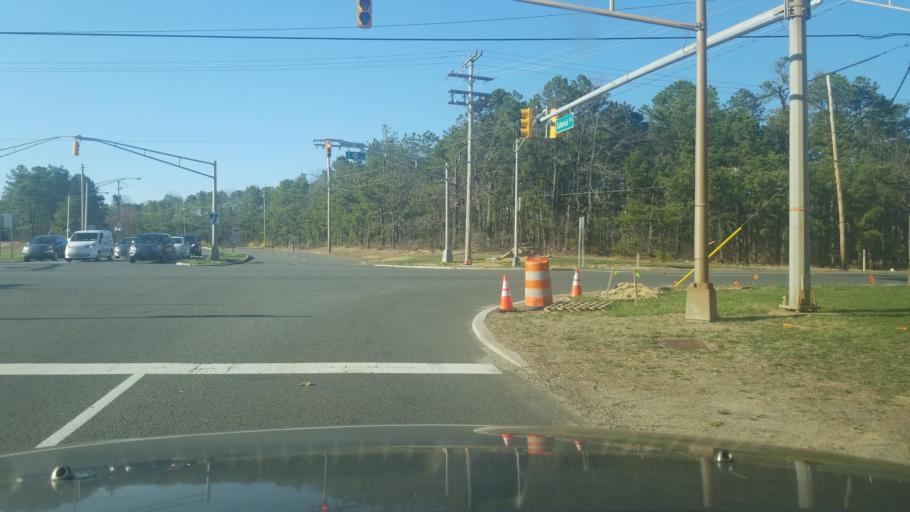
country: US
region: New Jersey
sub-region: Ocean County
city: Leisure Knoll
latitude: 40.0126
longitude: -74.2928
